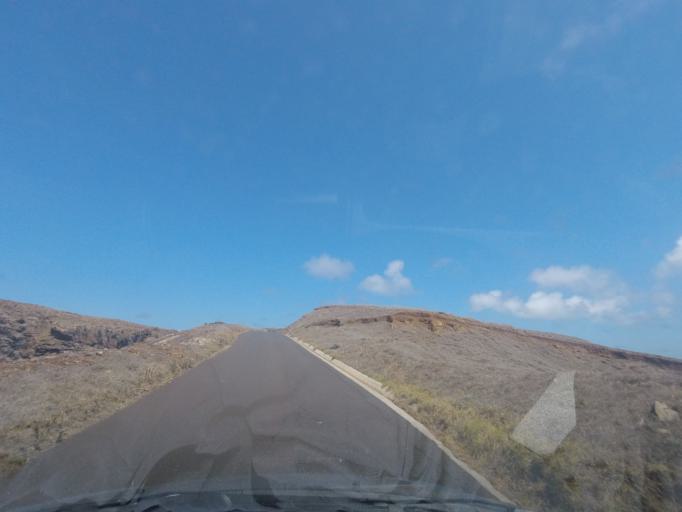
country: PT
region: Madeira
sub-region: Machico
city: Canical
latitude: 32.7487
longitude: -16.7124
